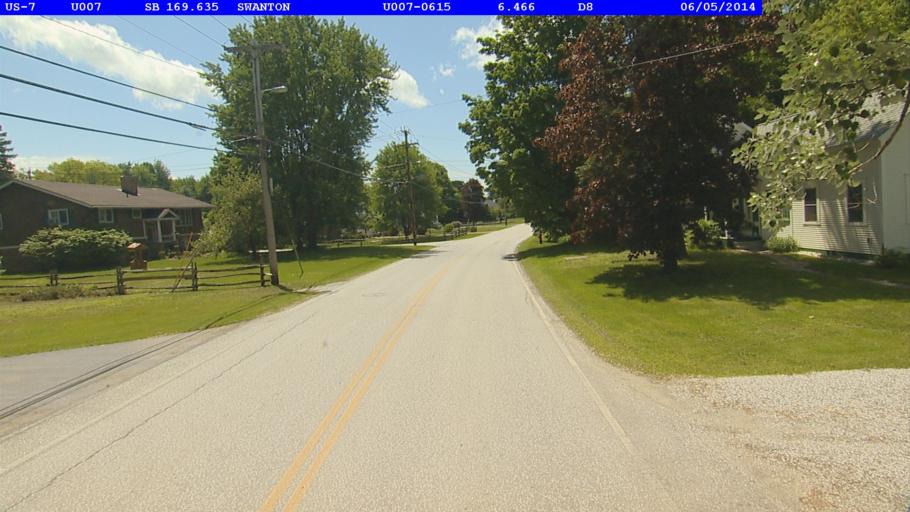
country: US
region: Vermont
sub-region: Franklin County
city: Swanton
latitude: 44.9263
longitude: -73.1200
